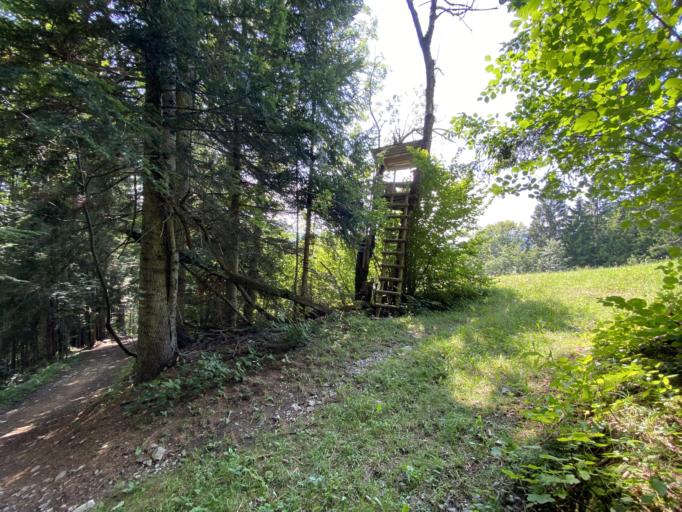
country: AT
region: Lower Austria
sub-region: Politischer Bezirk Lilienfeld
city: Annaberg
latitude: 47.8792
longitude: 15.3602
